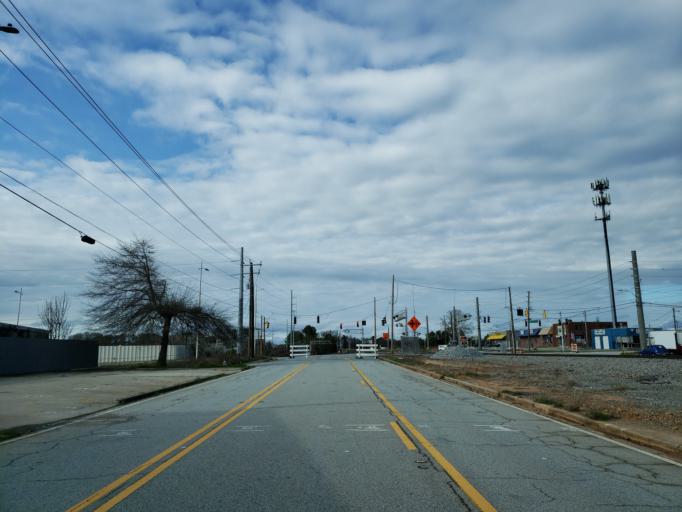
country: US
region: Georgia
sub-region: Fulton County
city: Hapeville
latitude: 33.6411
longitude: -84.3905
